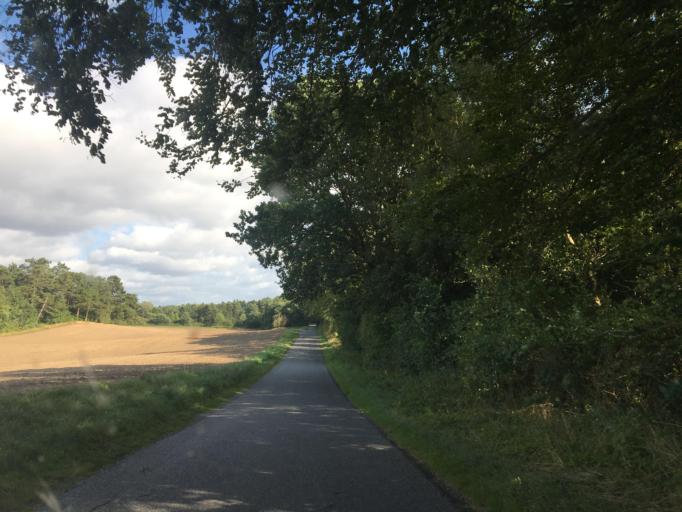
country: DK
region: South Denmark
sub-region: Middelfart Kommune
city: Ejby
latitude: 55.3932
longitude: 9.9261
